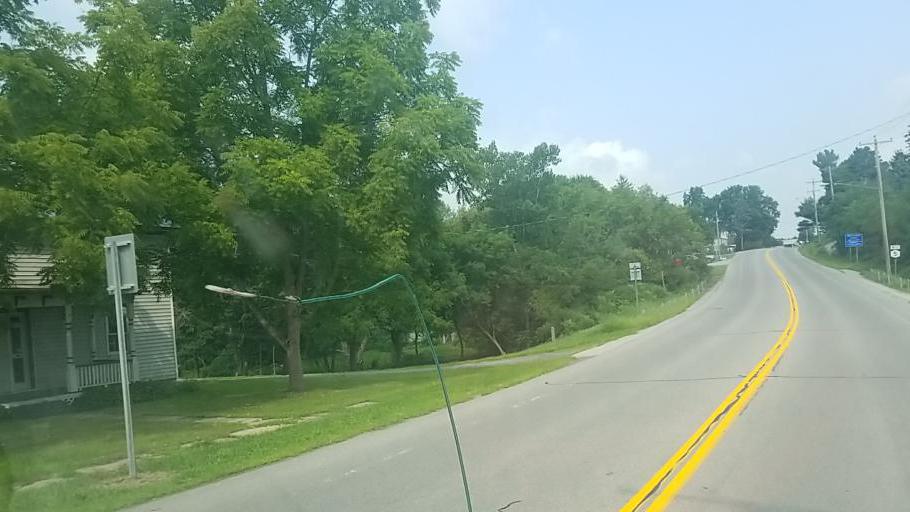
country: US
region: New York
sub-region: Montgomery County
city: Fort Plain
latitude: 42.9370
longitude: -74.6152
